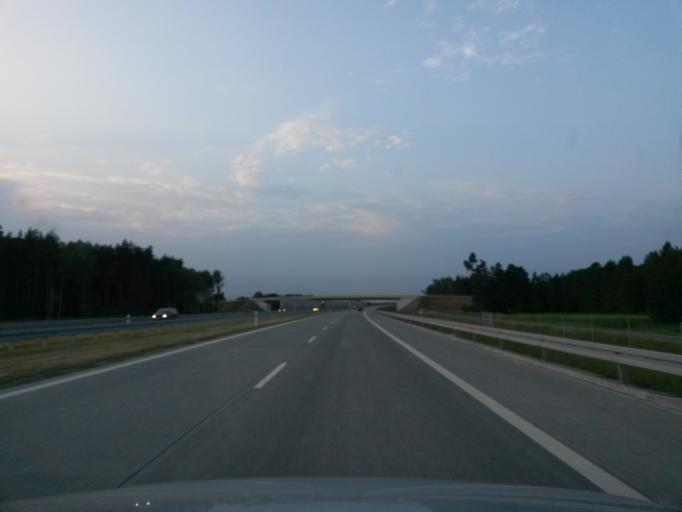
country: PL
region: Lodz Voivodeship
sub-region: Powiat sieradzki
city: Brzeznio
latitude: 51.4526
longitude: 18.6481
